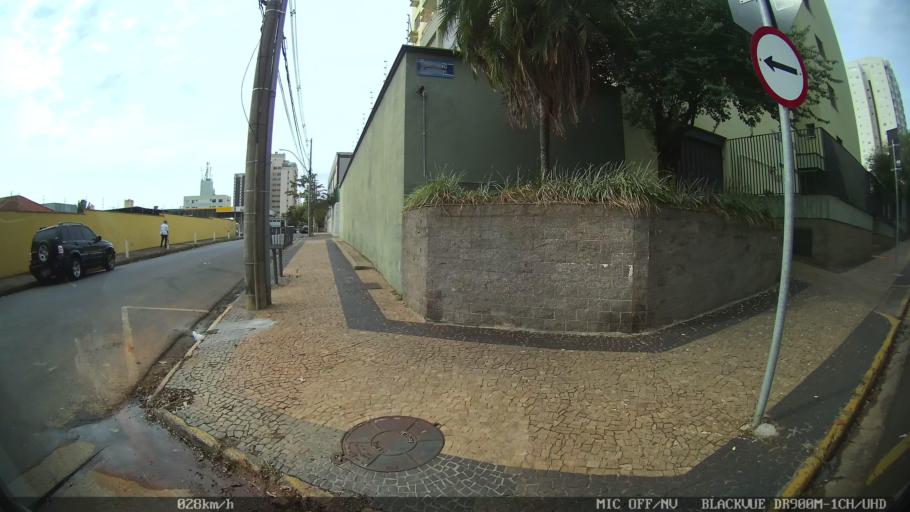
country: BR
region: Sao Paulo
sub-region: Piracicaba
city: Piracicaba
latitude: -22.7241
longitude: -47.6358
